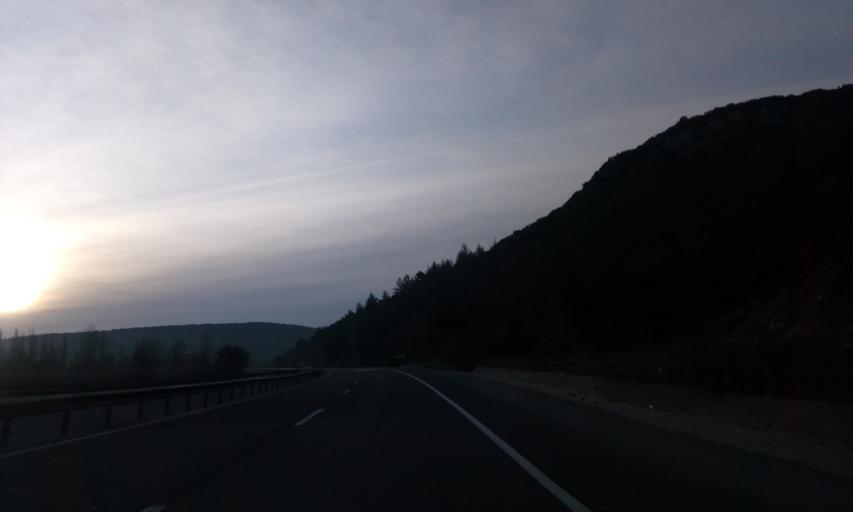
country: TR
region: Bilecik
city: Bilecik
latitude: 40.1517
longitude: 30.0221
